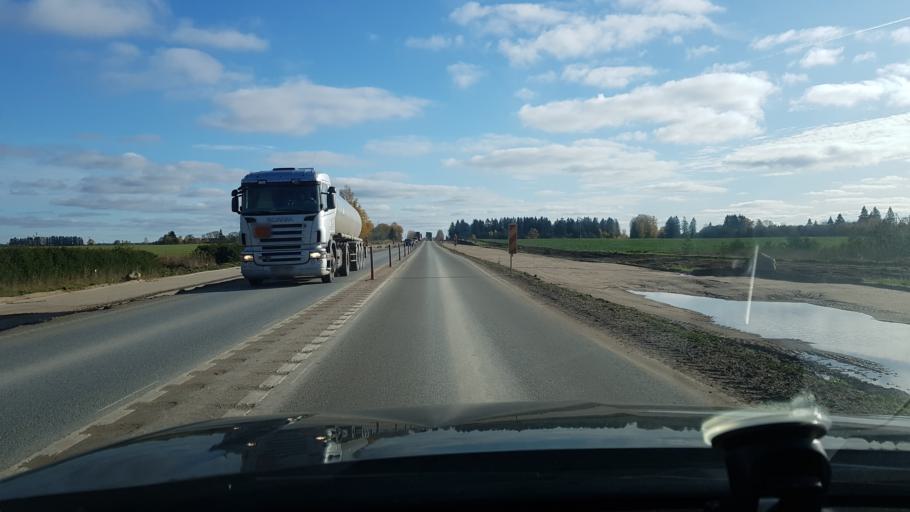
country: EE
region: Laeaene-Virumaa
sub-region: Kadrina vald
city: Kadrina
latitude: 59.4366
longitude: 26.1555
